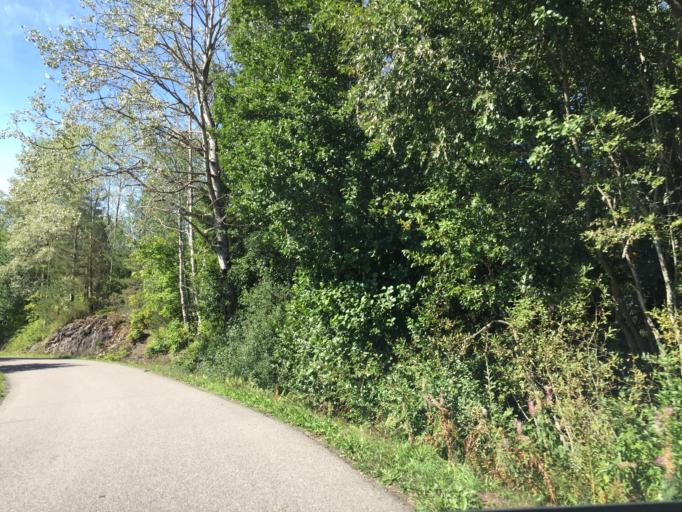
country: NO
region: Vestfold
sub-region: Hof
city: Hof
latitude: 59.4755
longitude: 10.1455
